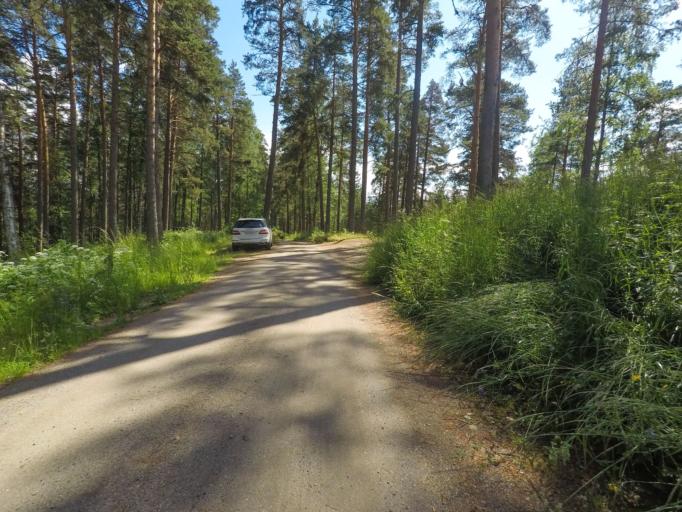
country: FI
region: Southern Savonia
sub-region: Savonlinna
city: Punkaharju
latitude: 61.8007
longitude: 29.3080
